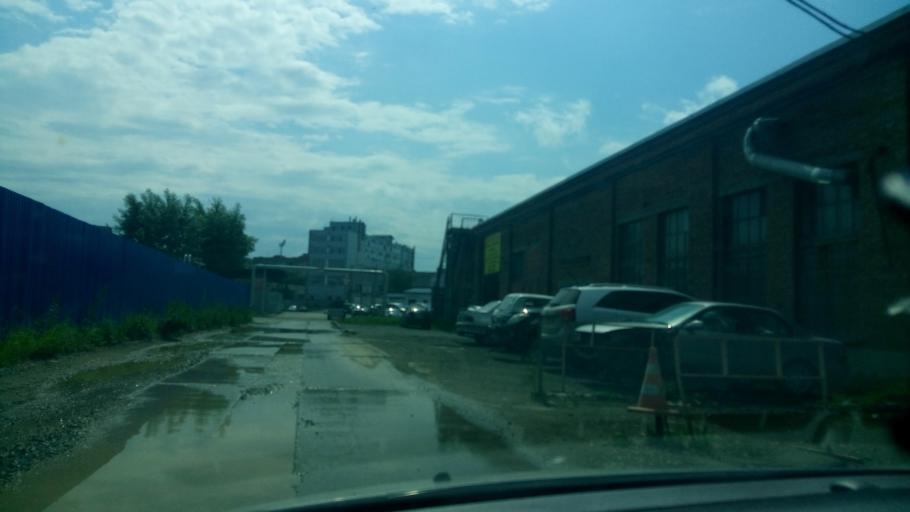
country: RU
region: Sverdlovsk
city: Yekaterinburg
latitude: 56.8578
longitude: 60.6608
